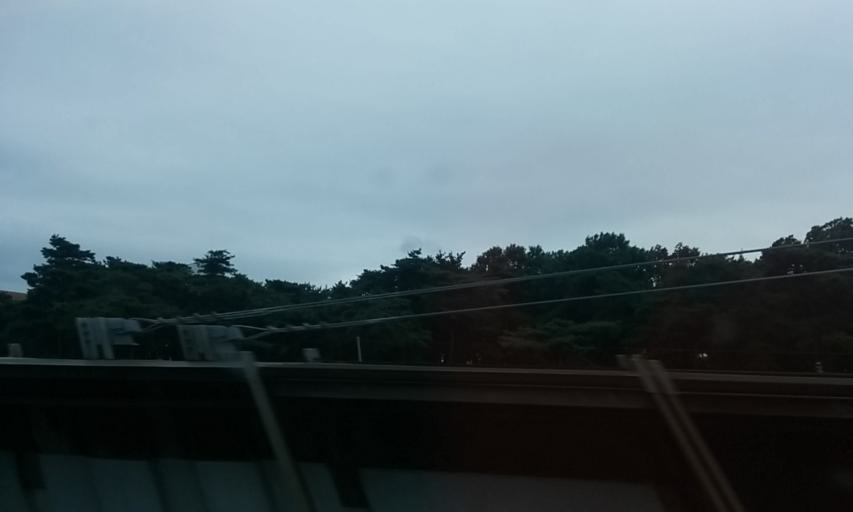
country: JP
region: Tochigi
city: Mibu
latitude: 36.3990
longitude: 139.8564
